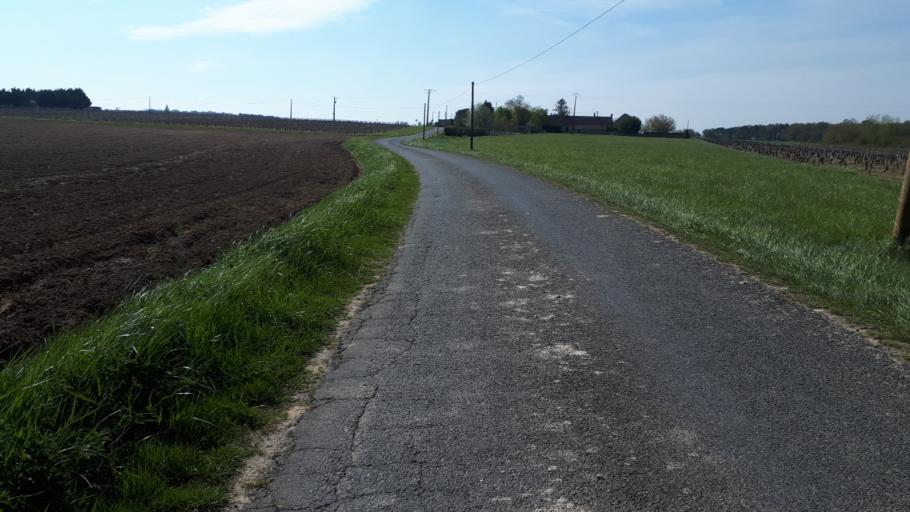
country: FR
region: Centre
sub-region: Departement du Loir-et-Cher
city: Saint-Romain-sur-Cher
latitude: 47.3686
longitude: 1.3896
